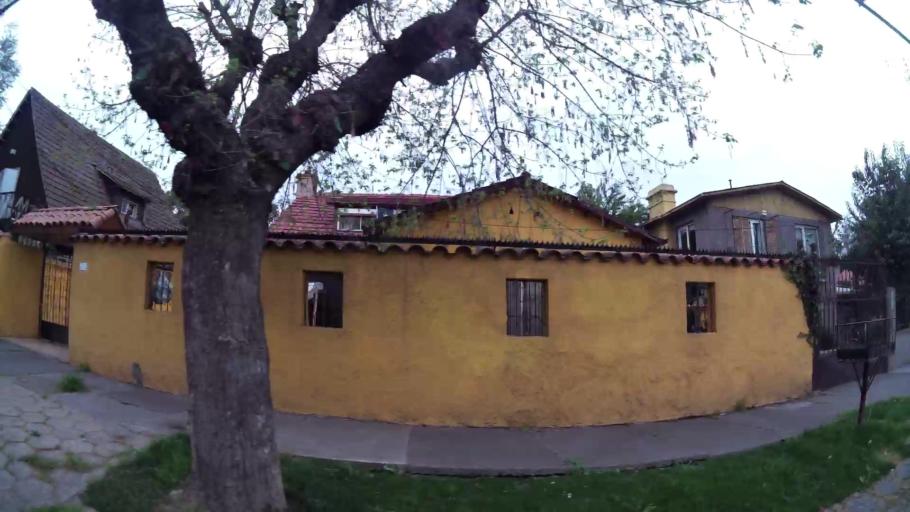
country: CL
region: Santiago Metropolitan
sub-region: Provincia de Santiago
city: Villa Presidente Frei, Nunoa, Santiago, Chile
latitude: -33.4605
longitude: -70.5912
